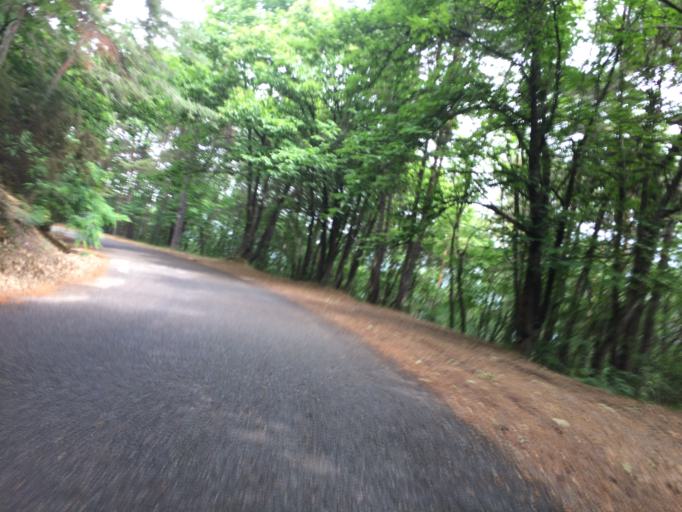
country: IT
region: Liguria
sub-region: Provincia di Imperia
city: Bajardo
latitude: 43.8823
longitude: 7.7403
